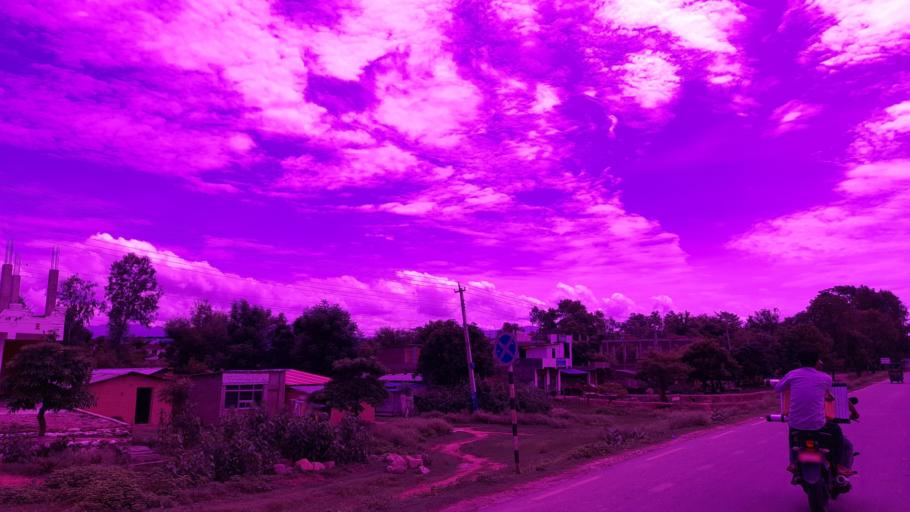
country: NP
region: Mid Western
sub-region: Bheri Zone
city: Nepalgunj
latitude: 28.1996
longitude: 81.6871
